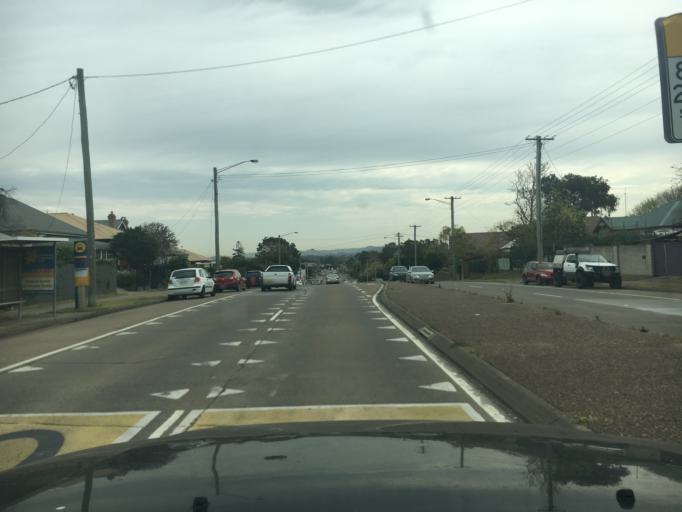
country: AU
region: New South Wales
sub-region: Maitland Municipality
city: East Maitland
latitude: -32.7520
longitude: 151.5860
